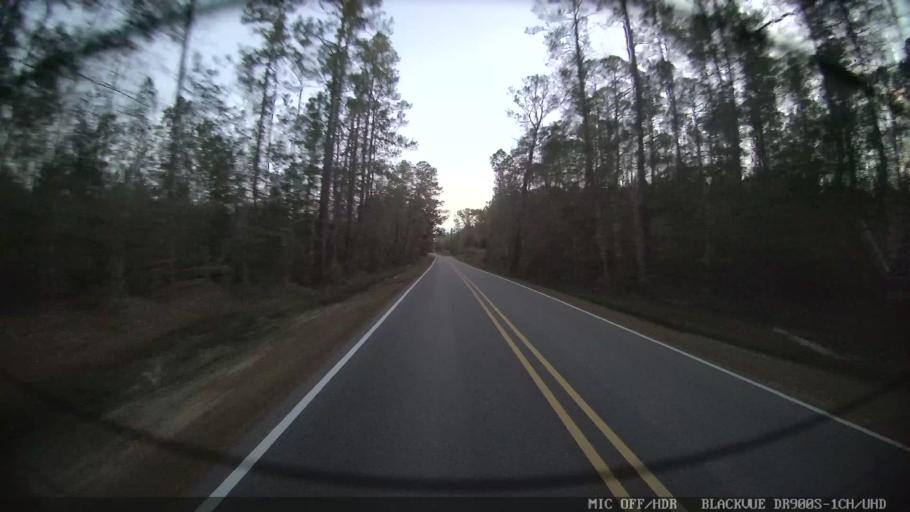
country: US
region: Mississippi
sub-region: Perry County
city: New Augusta
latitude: 31.0830
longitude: -89.1884
